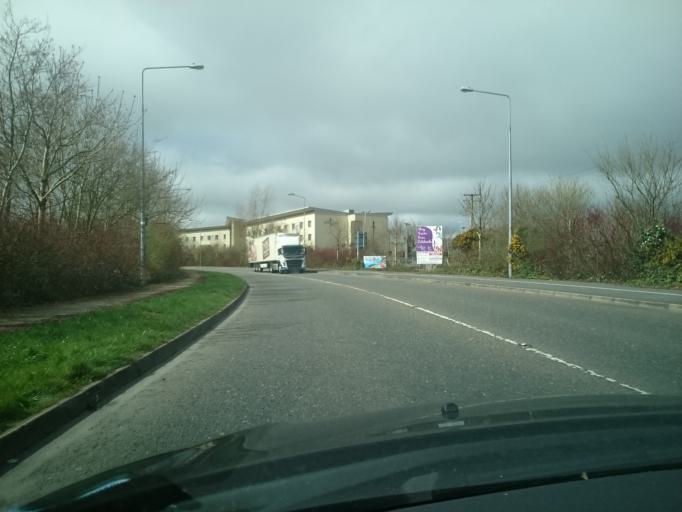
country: IE
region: Connaught
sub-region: Maigh Eo
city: Claremorris
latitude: 53.7251
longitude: -8.9875
